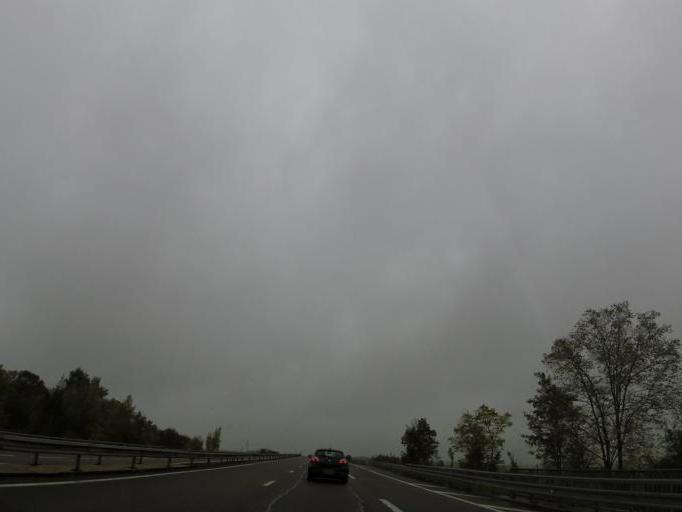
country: FR
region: Champagne-Ardenne
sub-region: Departement de la Marne
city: Courtisols
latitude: 49.0353
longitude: 4.4354
